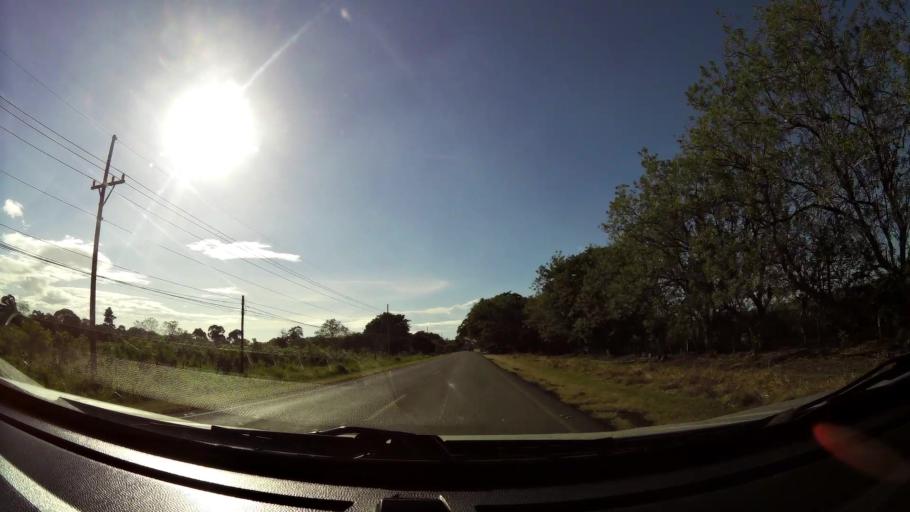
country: CR
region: Guanacaste
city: Belen
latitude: 10.4832
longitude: -85.5664
